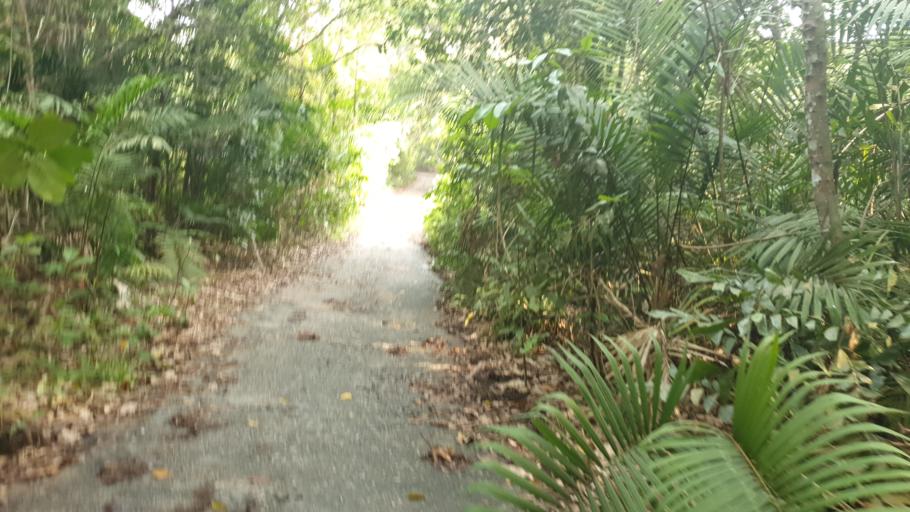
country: SG
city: Singapore
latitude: 1.3511
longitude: 103.8067
